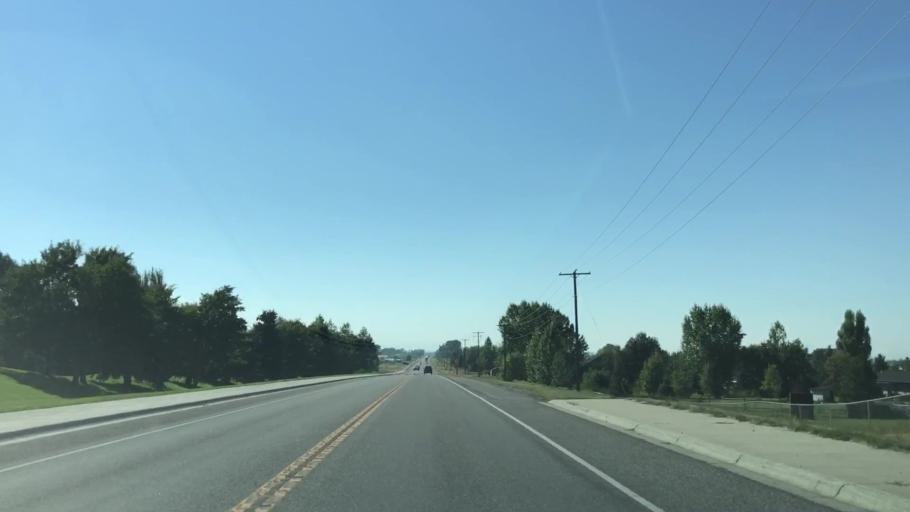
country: US
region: Montana
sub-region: Gallatin County
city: Belgrade
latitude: 45.7293
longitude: -111.1369
